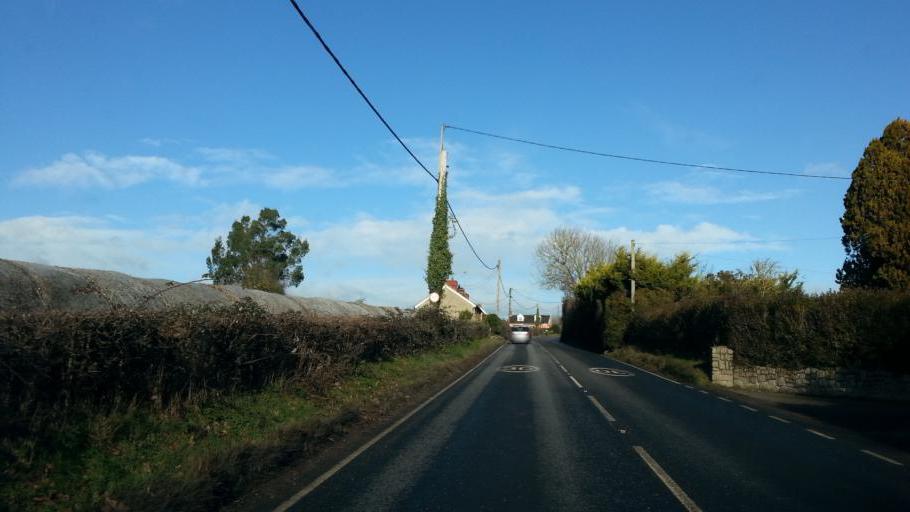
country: GB
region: England
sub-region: Suffolk
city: Halesworth
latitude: 52.3140
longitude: 1.5189
